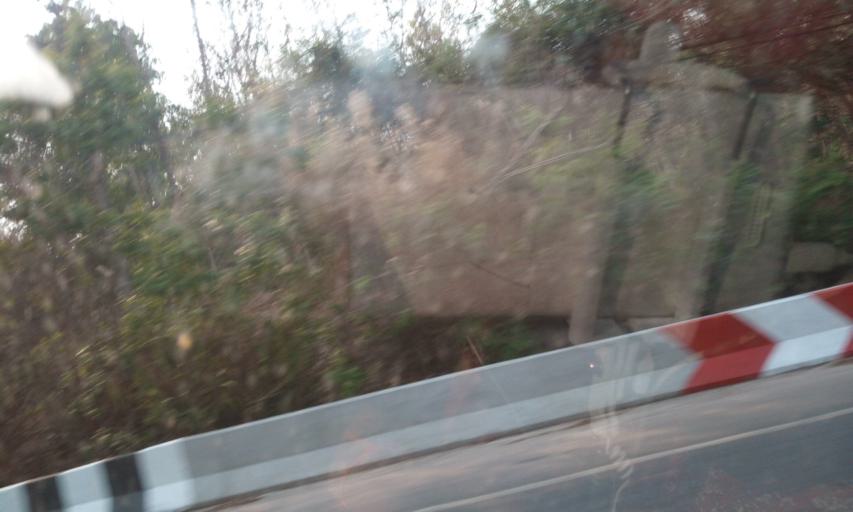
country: TH
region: Chiang Rai
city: Pa Daet
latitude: 19.6430
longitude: 99.9547
